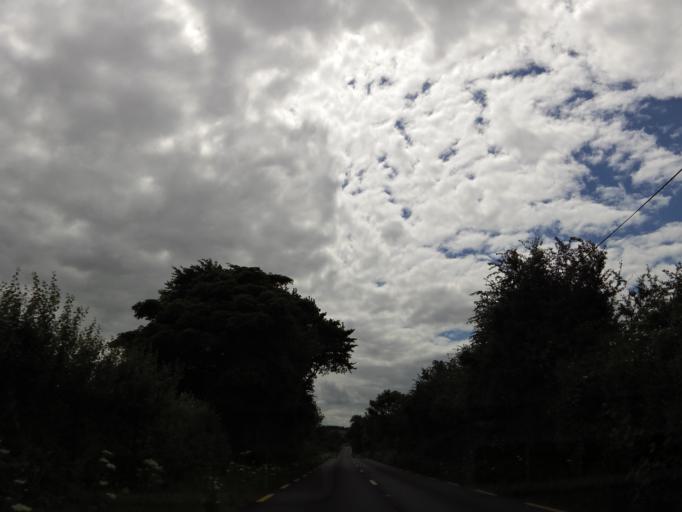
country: IE
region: Munster
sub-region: North Tipperary
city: Nenagh
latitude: 52.7791
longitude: -8.0308
